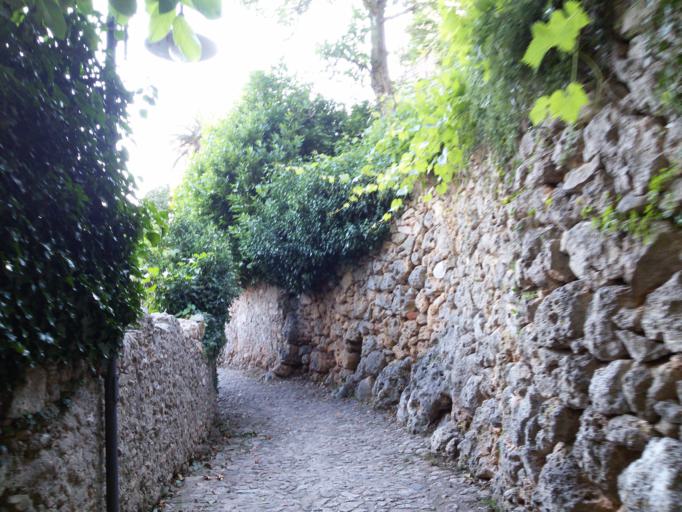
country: IT
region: Liguria
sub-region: Provincia di Savona
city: Borgio
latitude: 44.1703
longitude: 8.3127
